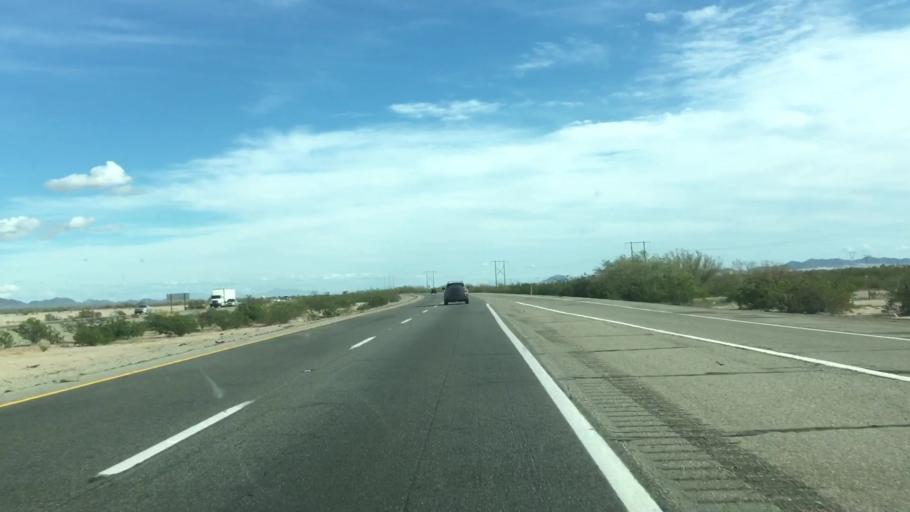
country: US
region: California
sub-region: Riverside County
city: Mesa Verde
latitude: 33.6068
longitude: -114.9875
